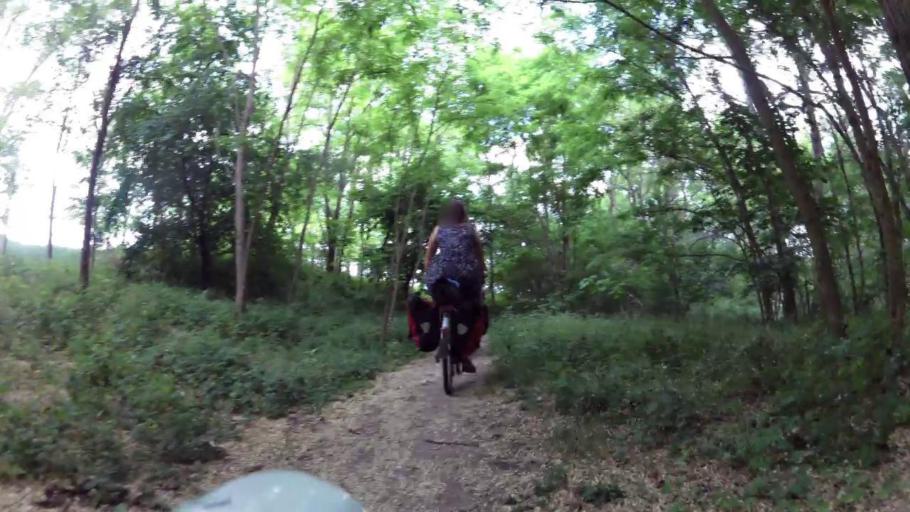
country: PL
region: Kujawsko-Pomorskie
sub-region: Bydgoszcz
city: Fordon
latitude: 53.1439
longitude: 18.1602
